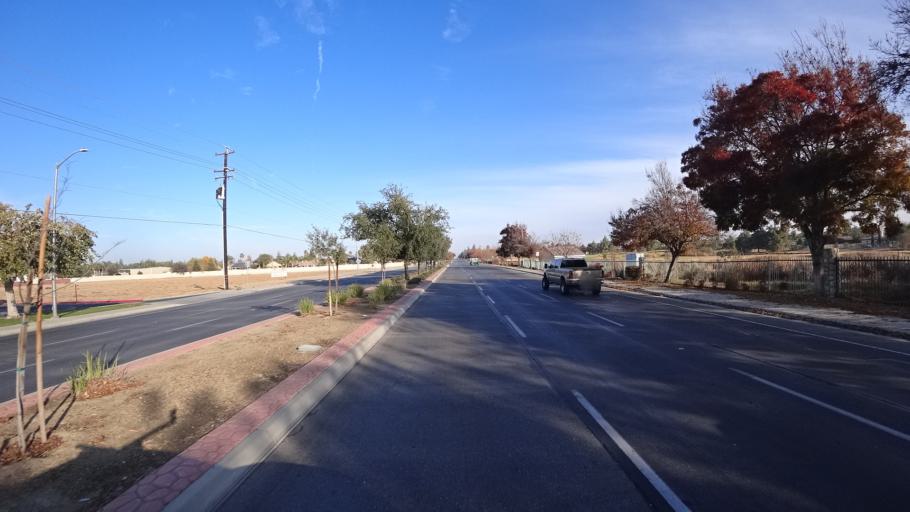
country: US
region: California
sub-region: Kern County
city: Greenacres
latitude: 35.4015
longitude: -119.1100
